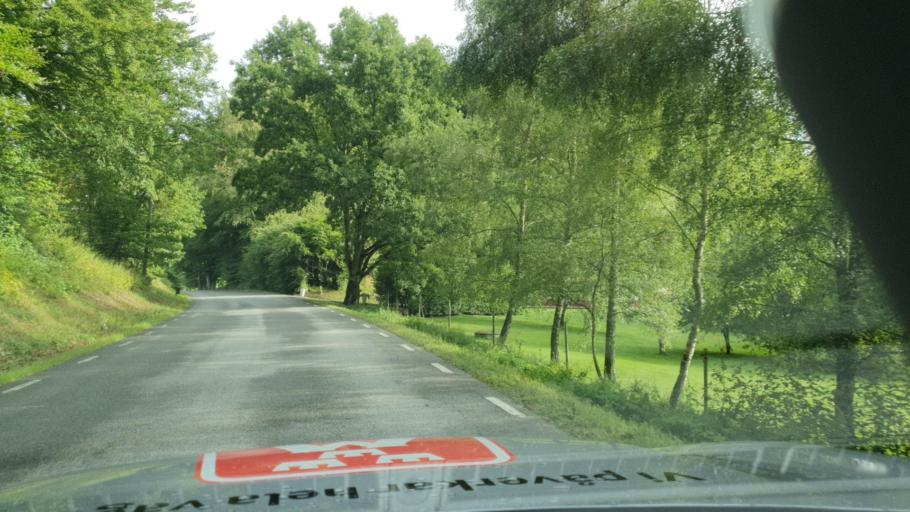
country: SE
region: Skane
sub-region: Hassleholms Kommun
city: Vinslov
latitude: 56.0880
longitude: 13.8499
